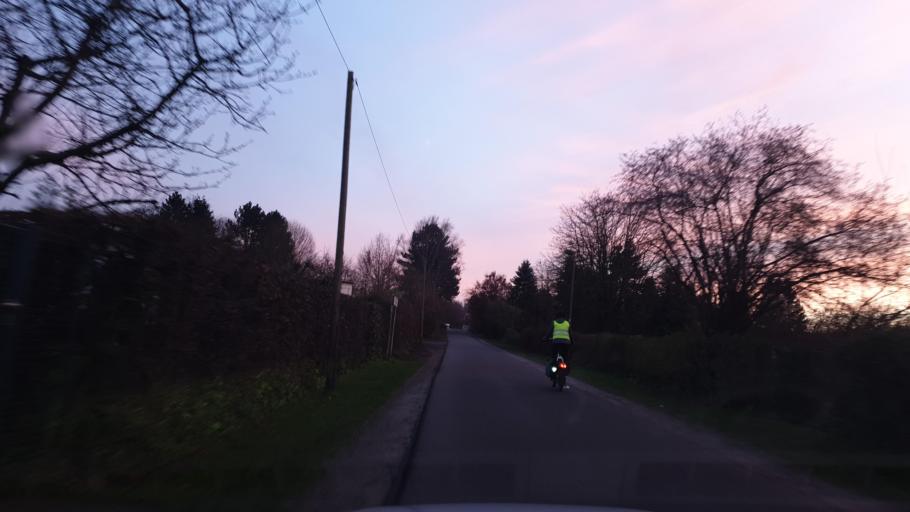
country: DE
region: Lower Saxony
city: Osnabrueck
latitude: 52.2563
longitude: 8.0346
